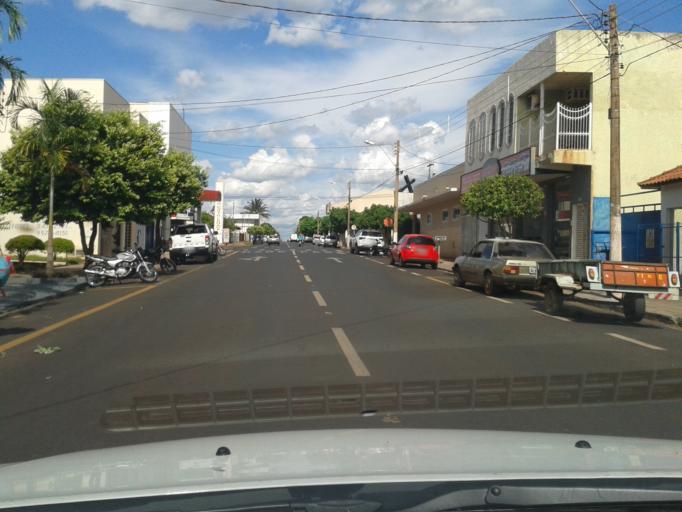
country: BR
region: Minas Gerais
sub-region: Iturama
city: Iturama
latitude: -19.7296
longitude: -50.1964
